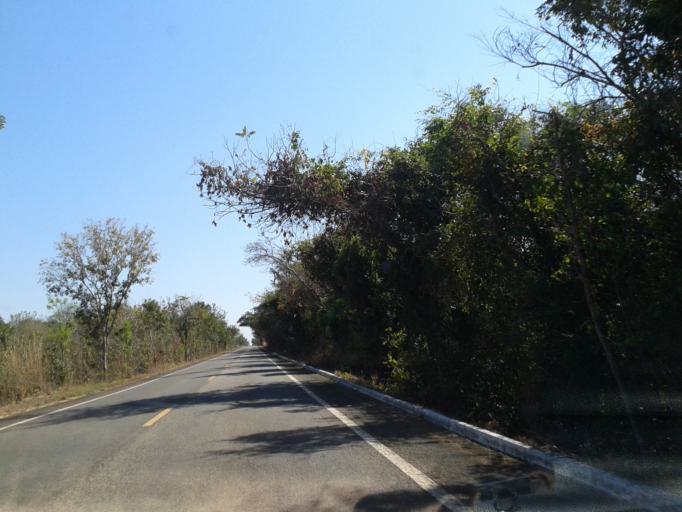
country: BR
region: Goias
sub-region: Sao Miguel Do Araguaia
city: Sao Miguel do Araguaia
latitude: -13.9307
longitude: -50.3208
